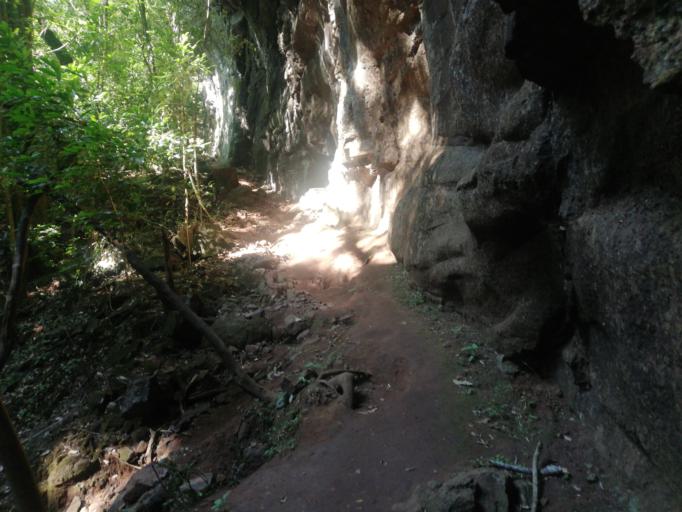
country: AR
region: Misiones
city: Cerro Azul
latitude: -27.7536
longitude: -55.5614
